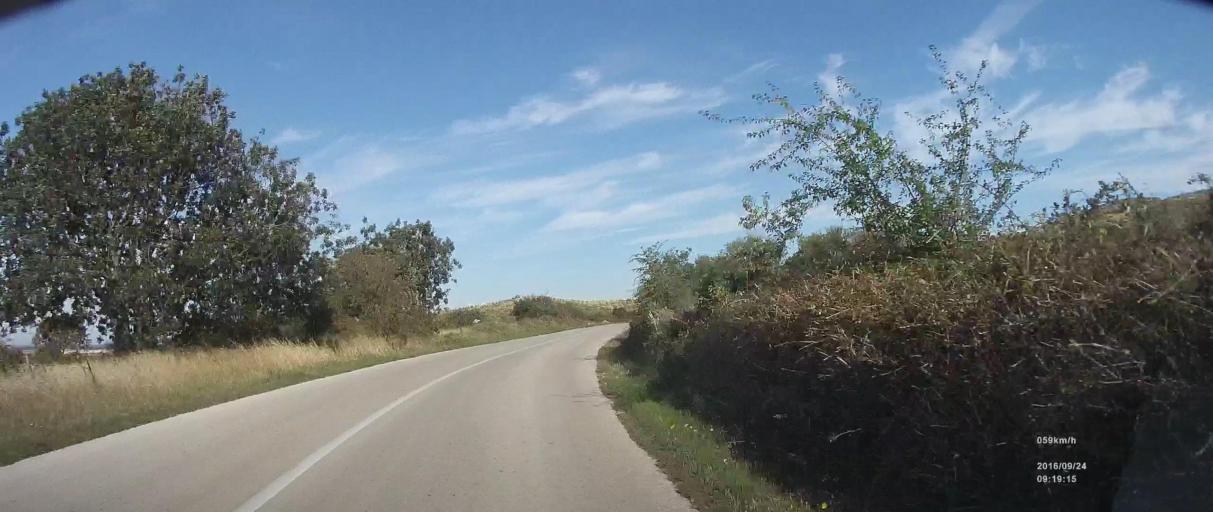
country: HR
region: Zadarska
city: Polaca
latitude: 44.0607
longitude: 15.5055
